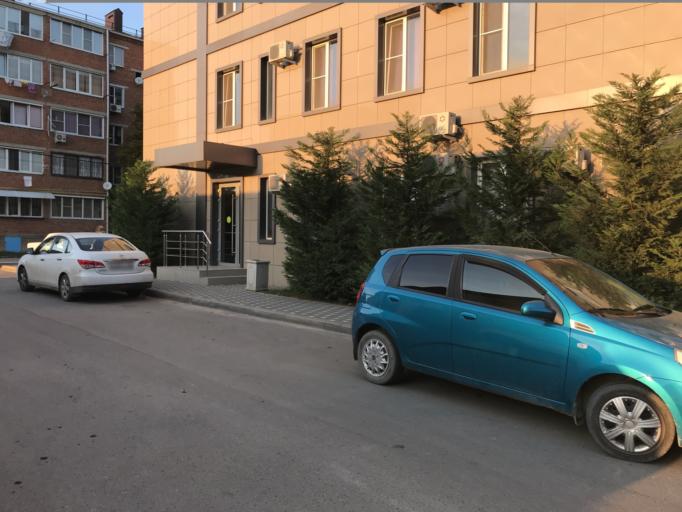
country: RU
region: Krasnodarskiy
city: Slavyansk-na-Kubani
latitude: 45.2583
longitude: 38.1221
